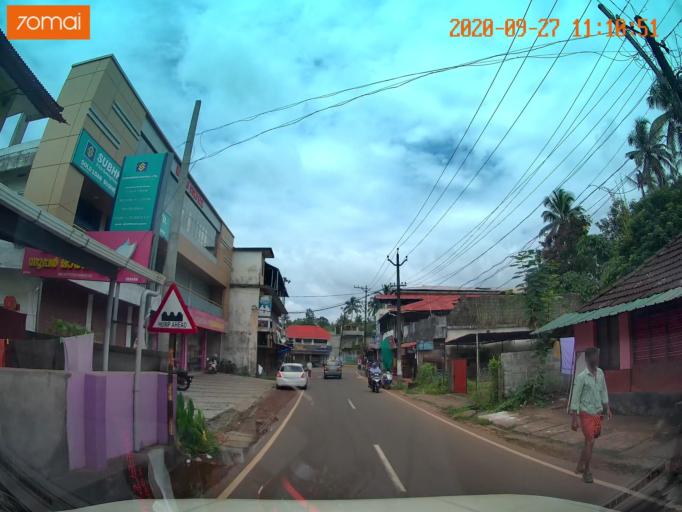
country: IN
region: Kerala
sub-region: Thrissur District
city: Thanniyam
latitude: 10.4310
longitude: 76.2174
